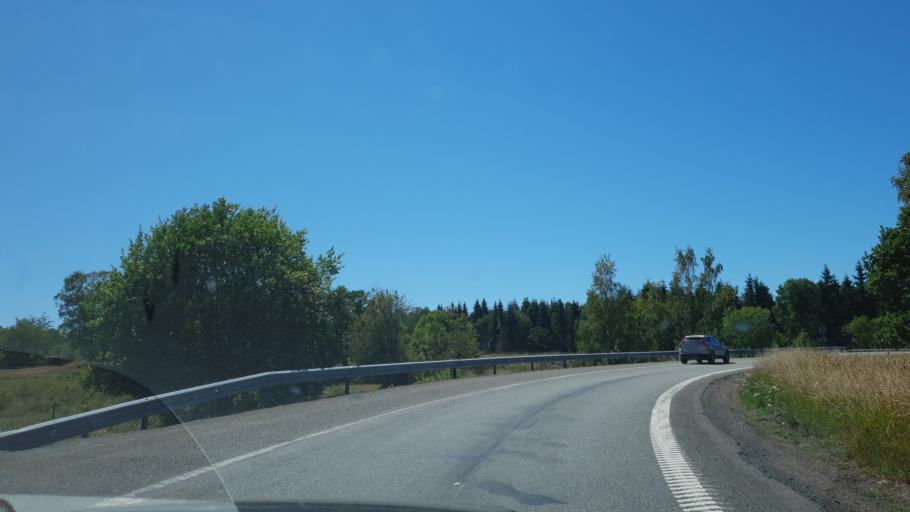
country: SE
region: Joenkoeping
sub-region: Jonkopings Kommun
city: Graenna
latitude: 57.9924
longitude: 14.4411
